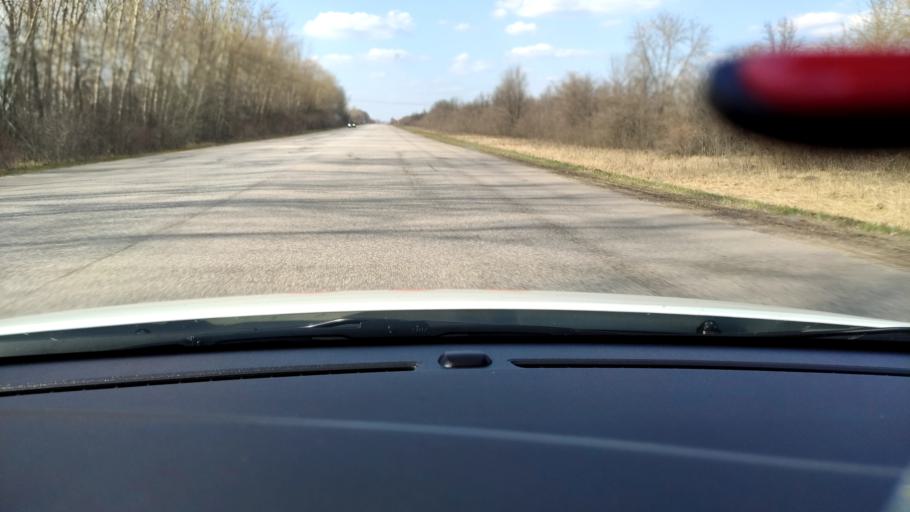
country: RU
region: Voronezj
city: Kolodeznyy
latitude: 51.2732
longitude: 39.0473
